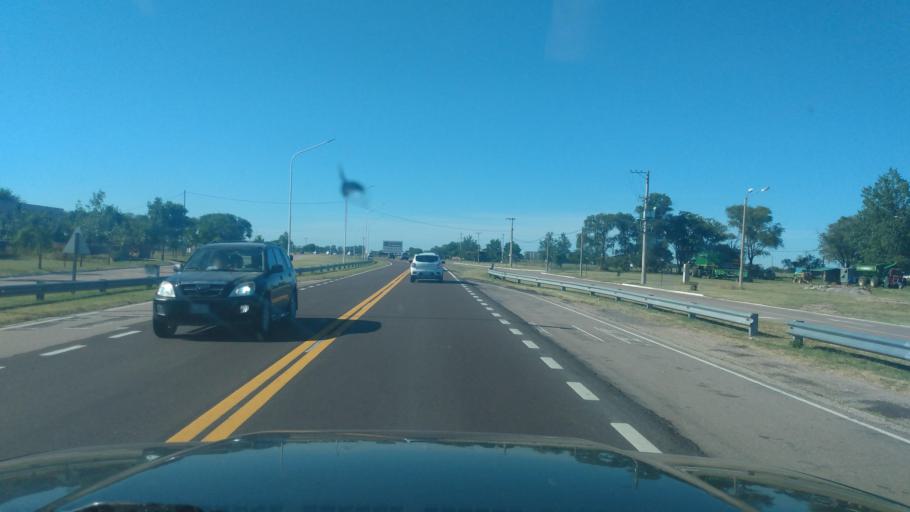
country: AR
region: La Pampa
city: Doblas
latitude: -37.0334
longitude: -64.2889
